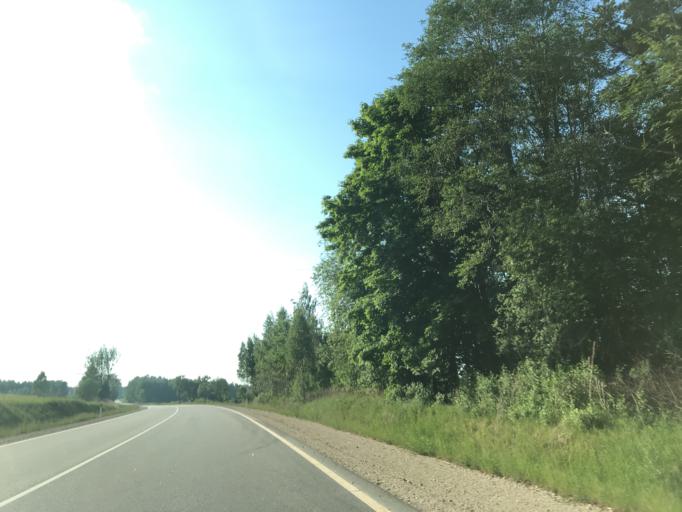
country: LV
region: Lielvarde
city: Lielvarde
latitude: 56.6924
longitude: 24.8345
